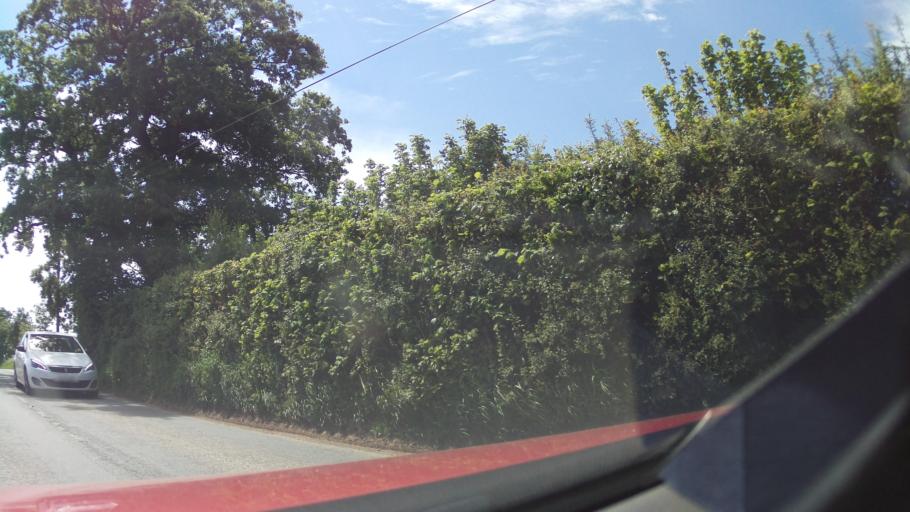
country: GB
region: England
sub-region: Devon
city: Uffculme
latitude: 50.8353
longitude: -3.3027
